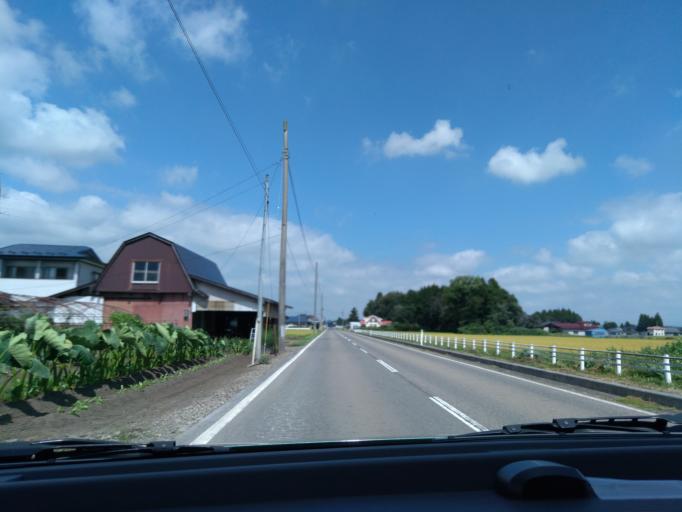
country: JP
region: Iwate
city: Kitakami
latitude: 39.3045
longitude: 141.0510
